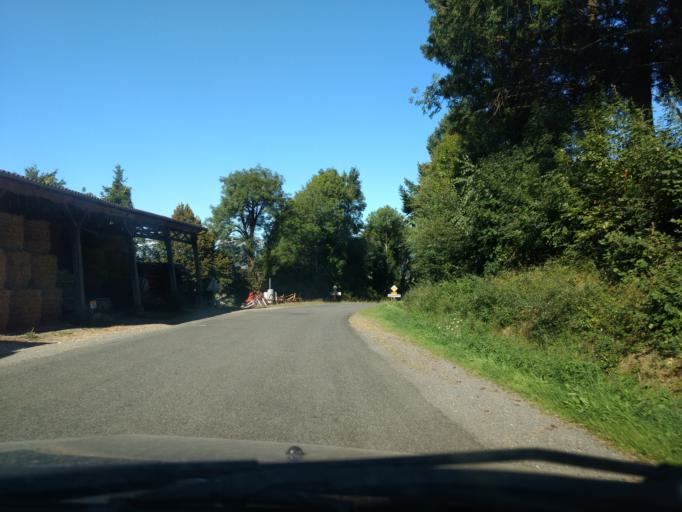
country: FR
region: Midi-Pyrenees
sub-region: Departement de l'Aveyron
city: Livinhac-le-Haut
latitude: 44.6171
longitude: 2.1943
